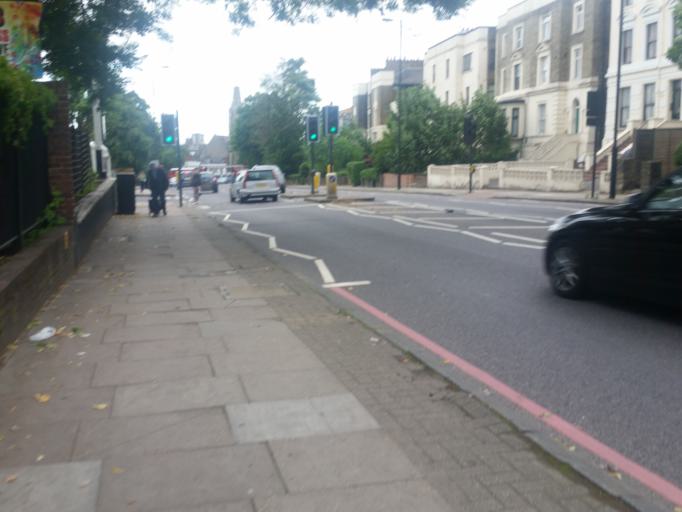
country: GB
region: England
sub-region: Greater London
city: Holloway
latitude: 51.5520
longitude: -0.1255
